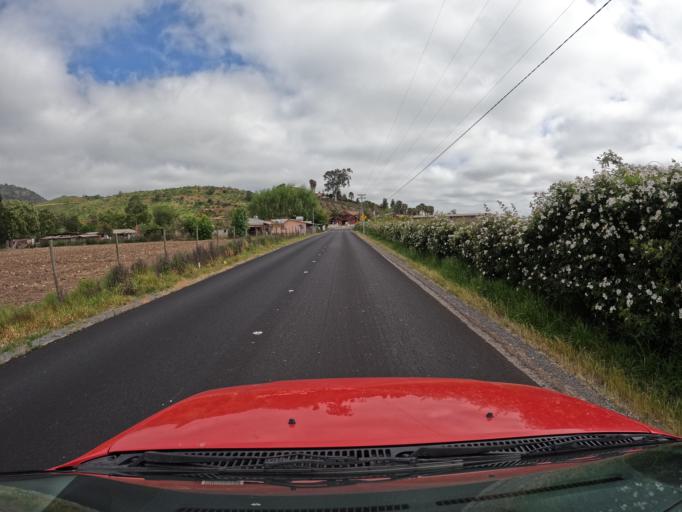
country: CL
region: O'Higgins
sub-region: Provincia de Colchagua
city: Santa Cruz
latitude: -34.6639
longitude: -71.3984
